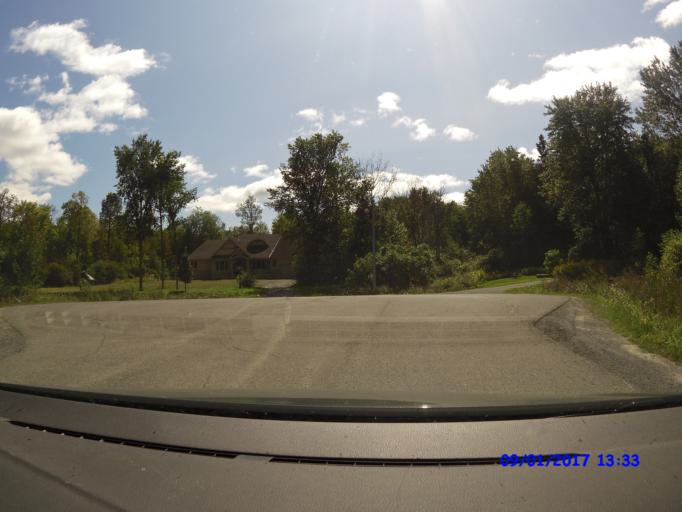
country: CA
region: Ontario
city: Bells Corners
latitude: 45.3526
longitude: -75.9983
